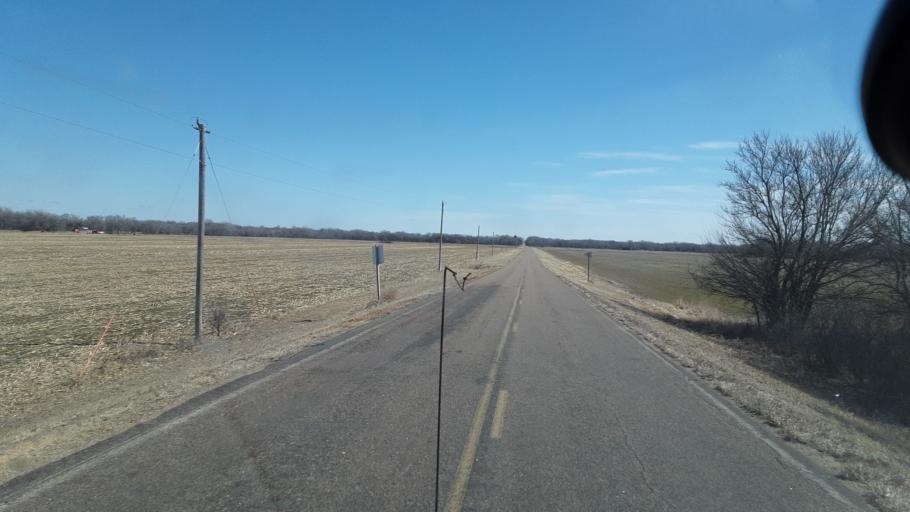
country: US
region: Kansas
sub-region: Reno County
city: Nickerson
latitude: 38.2174
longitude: -98.0592
